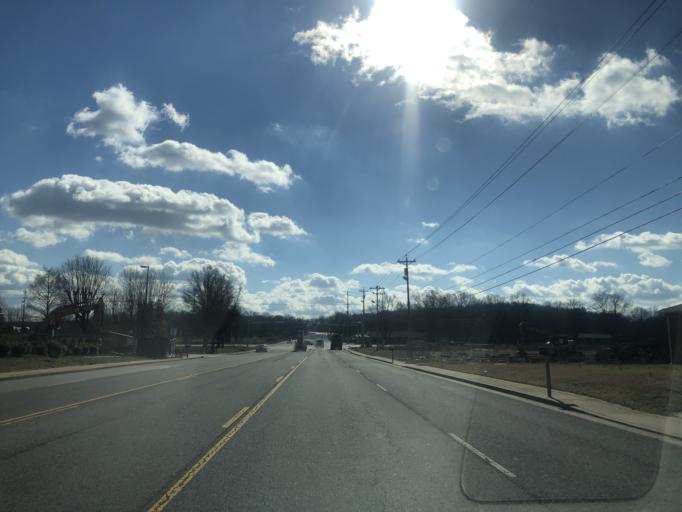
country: US
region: Tennessee
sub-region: Rutherford County
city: Murfreesboro
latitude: 35.8448
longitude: -86.4932
